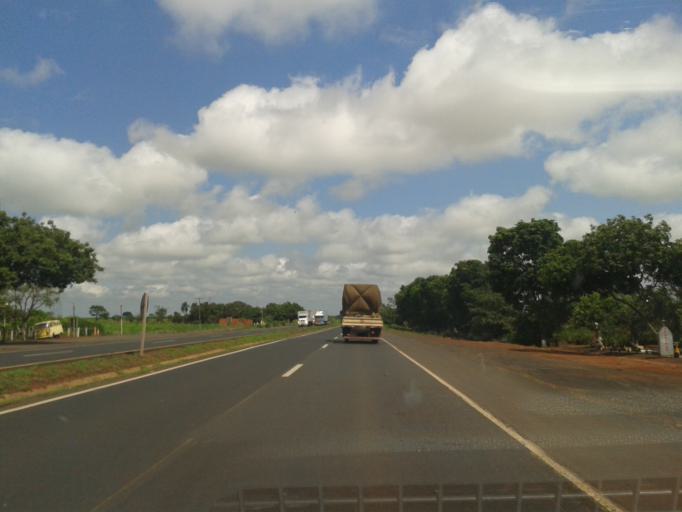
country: BR
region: Minas Gerais
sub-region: Centralina
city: Centralina
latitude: -18.7014
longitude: -49.1435
